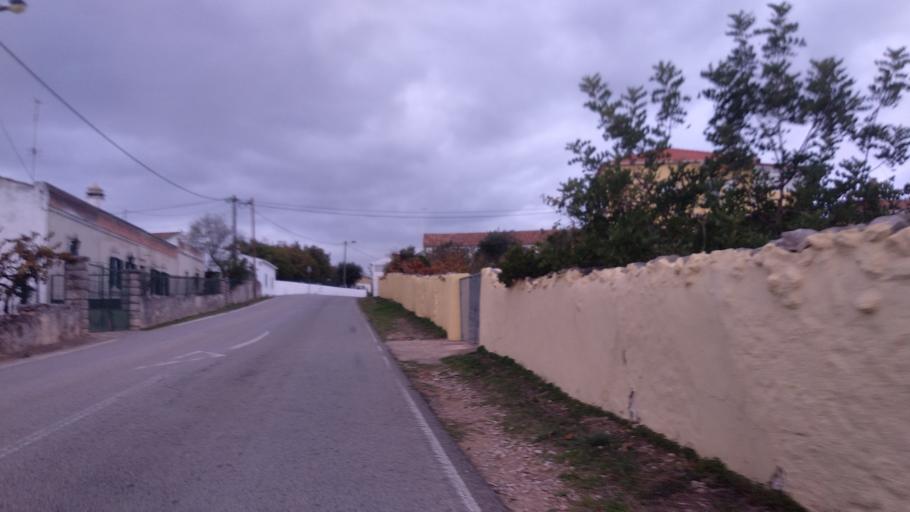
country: PT
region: Faro
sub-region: Sao Bras de Alportel
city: Sao Bras de Alportel
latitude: 37.1698
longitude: -7.9078
